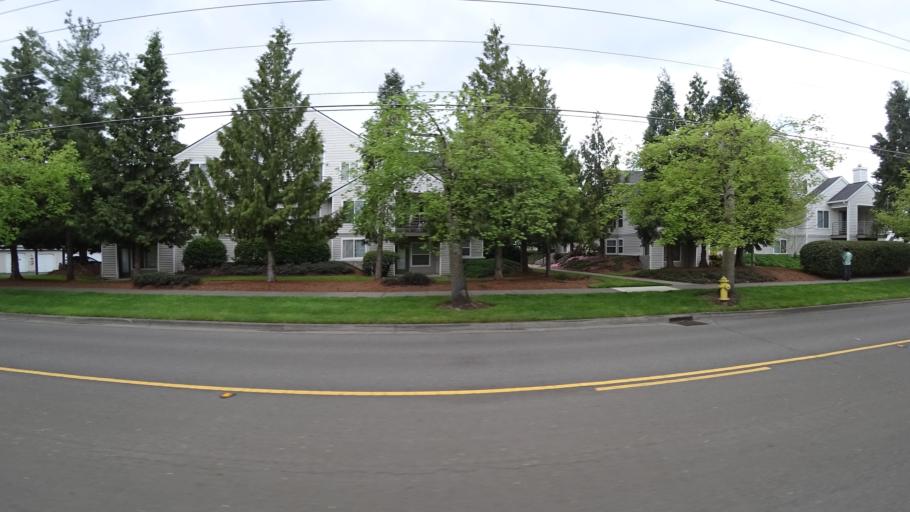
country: US
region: Oregon
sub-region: Washington County
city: Hillsboro
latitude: 45.5437
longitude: -122.9663
